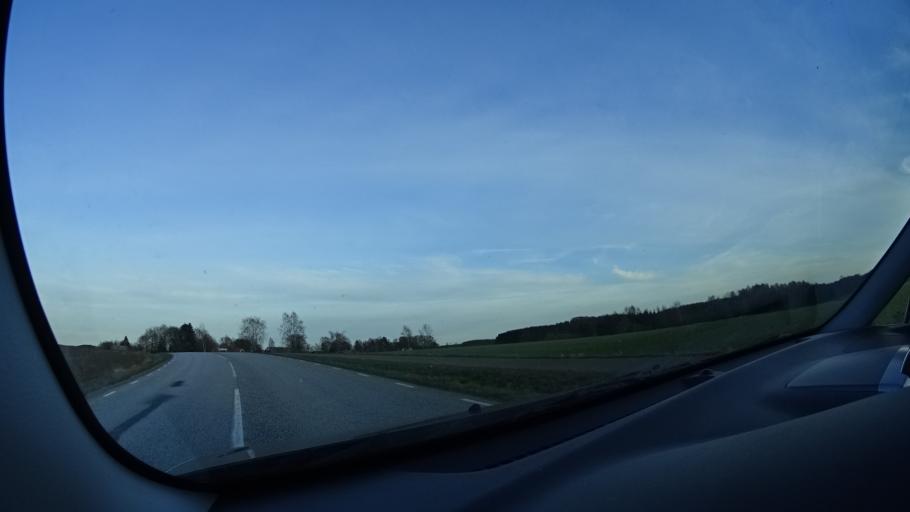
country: SE
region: Skane
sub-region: Eslovs Kommun
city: Stehag
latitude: 55.9462
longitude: 13.3539
